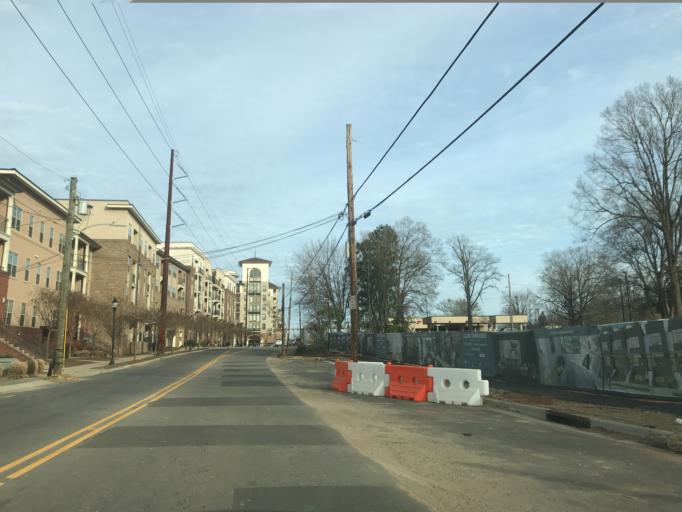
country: US
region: North Carolina
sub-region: Wake County
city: West Raleigh
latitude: 35.7895
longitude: -78.6649
